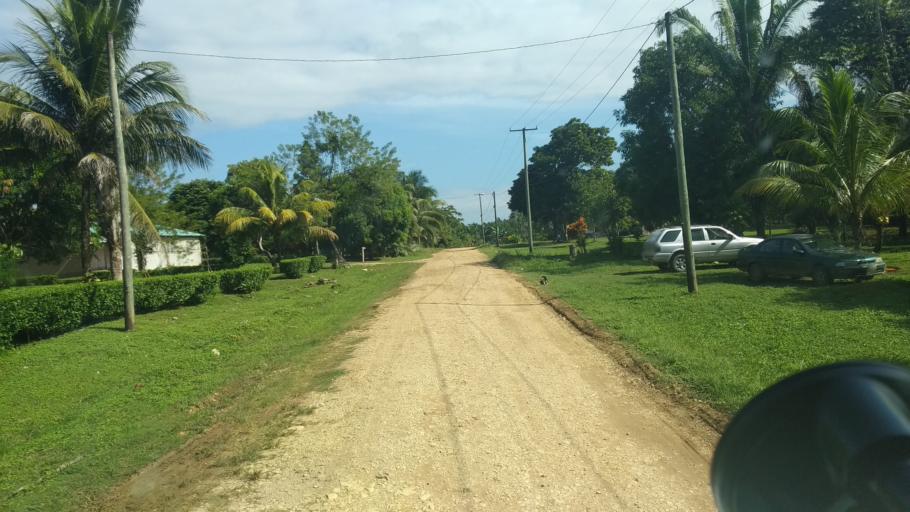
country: BZ
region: Toledo
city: Punta Gorda
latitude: 16.2126
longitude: -88.9106
